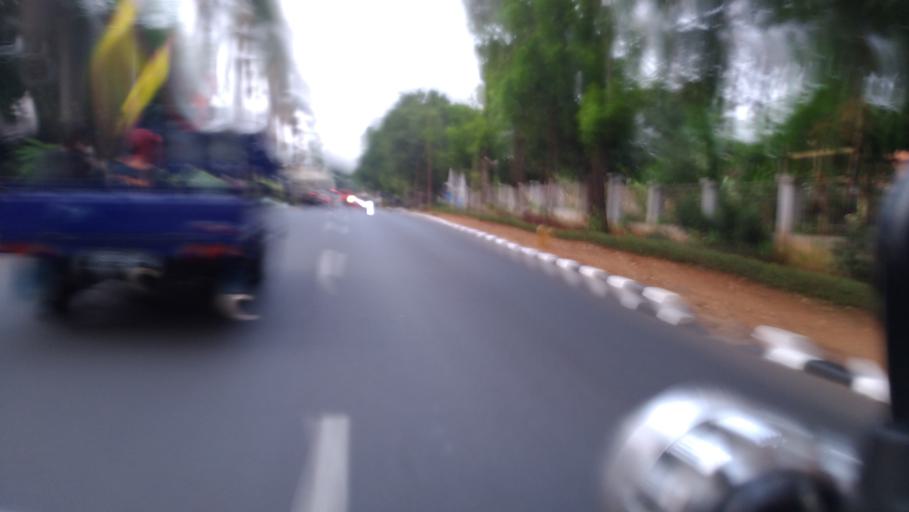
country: ID
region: West Java
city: Cileungsir
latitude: -6.3587
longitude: 106.8894
